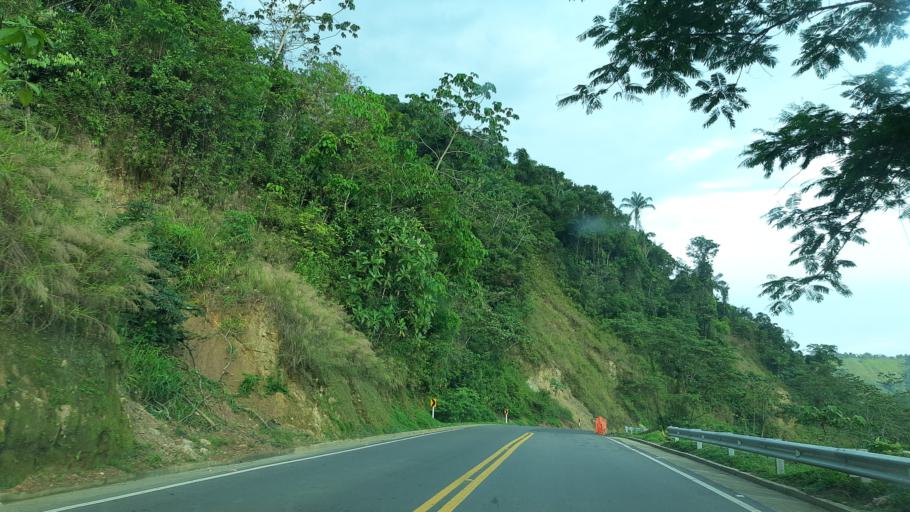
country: CO
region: Boyaca
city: San Luis de Gaceno
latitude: 4.8310
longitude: -73.1518
